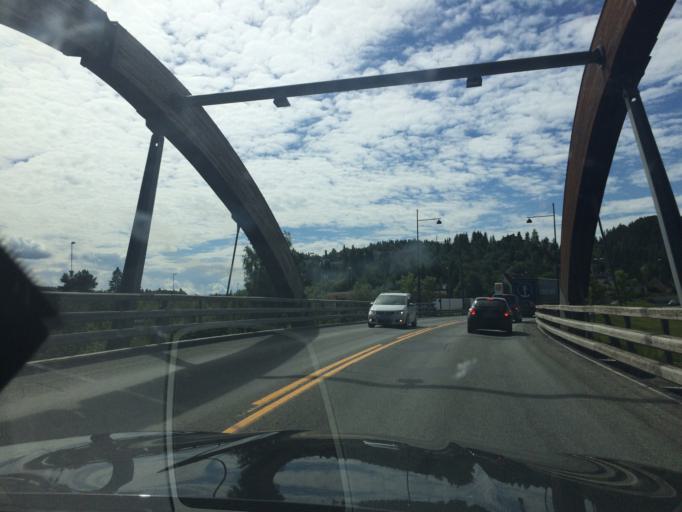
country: NO
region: Nord-Trondelag
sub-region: Steinkjer
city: Steinkjer
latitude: 64.0062
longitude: 11.4995
